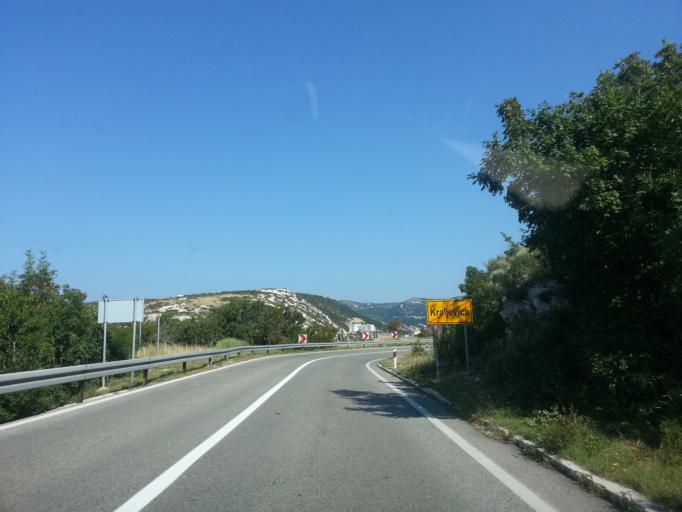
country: HR
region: Primorsko-Goranska
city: Kraljevica
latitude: 45.2804
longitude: 14.5657
